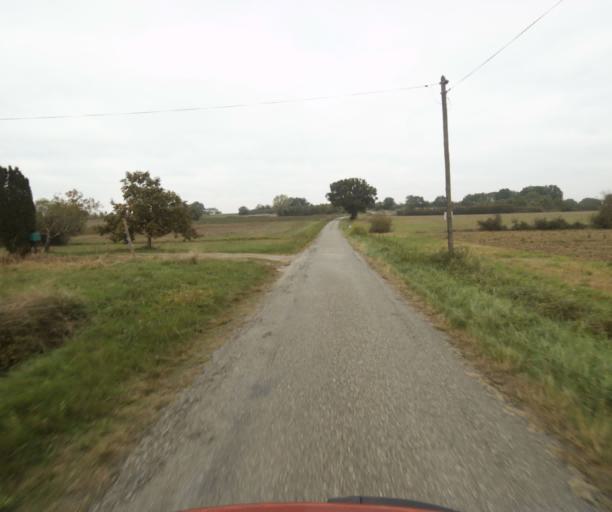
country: FR
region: Midi-Pyrenees
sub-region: Departement du Tarn-et-Garonne
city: Verdun-sur-Garonne
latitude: 43.8164
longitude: 1.2065
